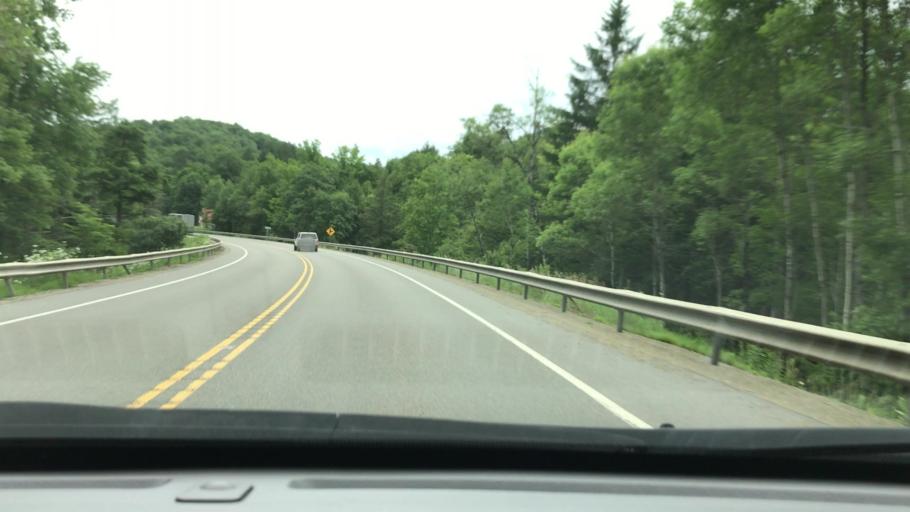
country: US
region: Pennsylvania
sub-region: McKean County
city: Kane
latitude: 41.6698
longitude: -78.6802
